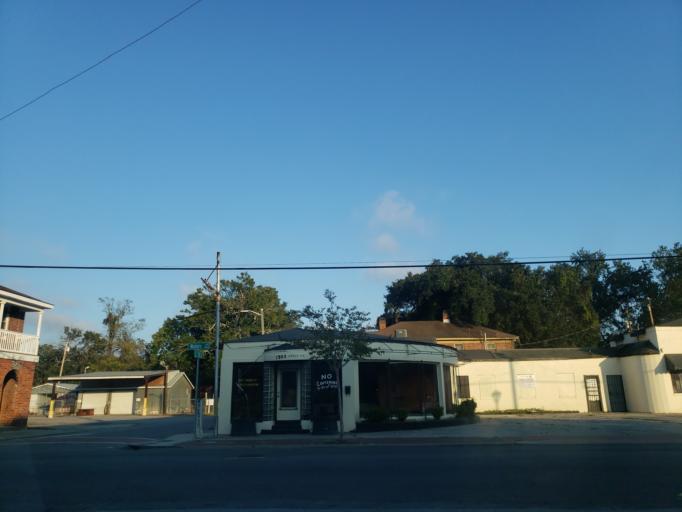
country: US
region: Georgia
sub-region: Chatham County
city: Savannah
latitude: 32.0547
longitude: -81.0833
